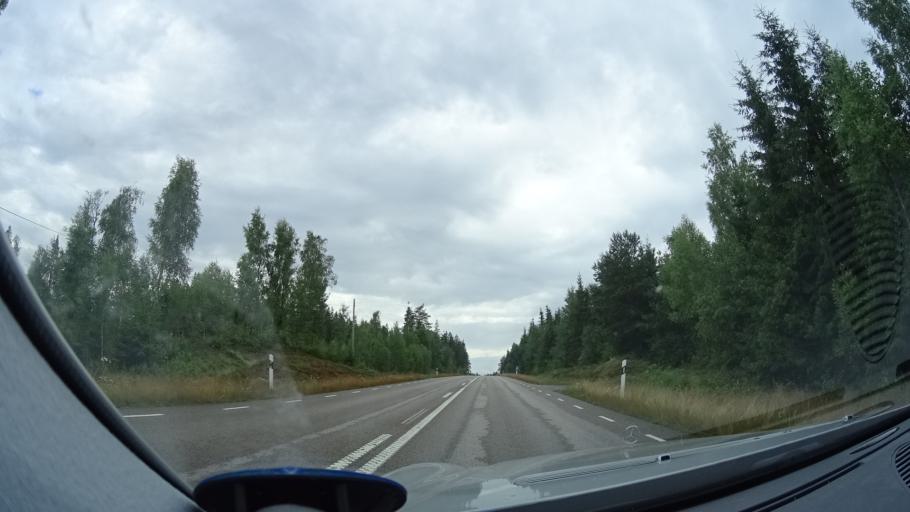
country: SE
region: Kronoberg
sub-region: Tingsryds Kommun
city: Tingsryd
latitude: 56.4492
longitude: 14.9887
